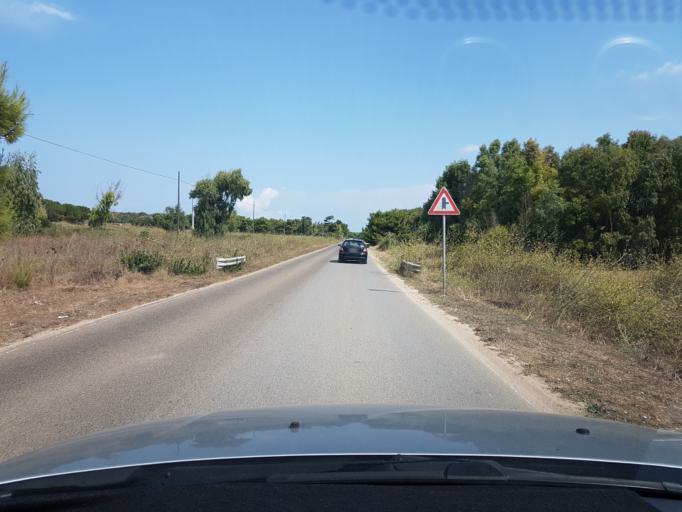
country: IT
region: Sardinia
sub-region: Provincia di Oristano
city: Cabras
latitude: 39.8904
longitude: 8.4350
